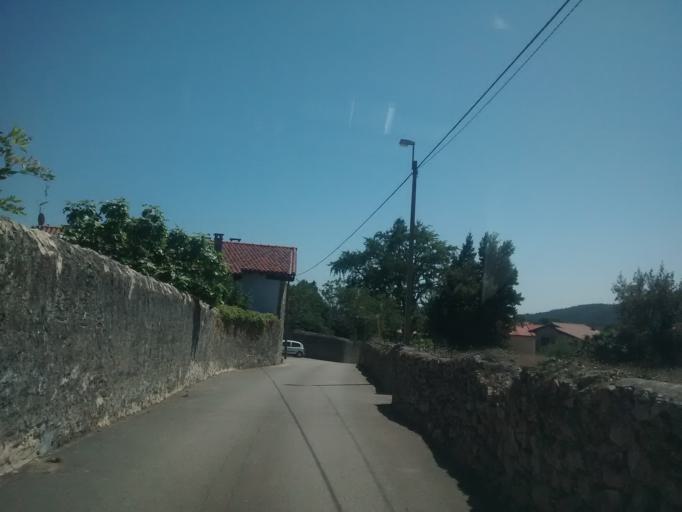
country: ES
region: Cantabria
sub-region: Provincia de Cantabria
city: Arnuero
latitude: 43.4760
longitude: -3.5657
